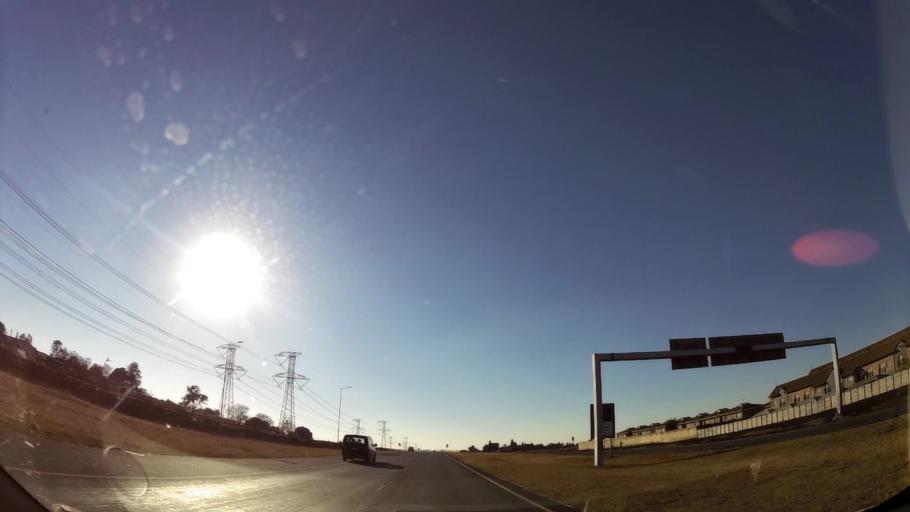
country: ZA
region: Gauteng
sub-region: City of Johannesburg Metropolitan Municipality
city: Modderfontein
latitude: -26.0889
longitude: 28.1932
